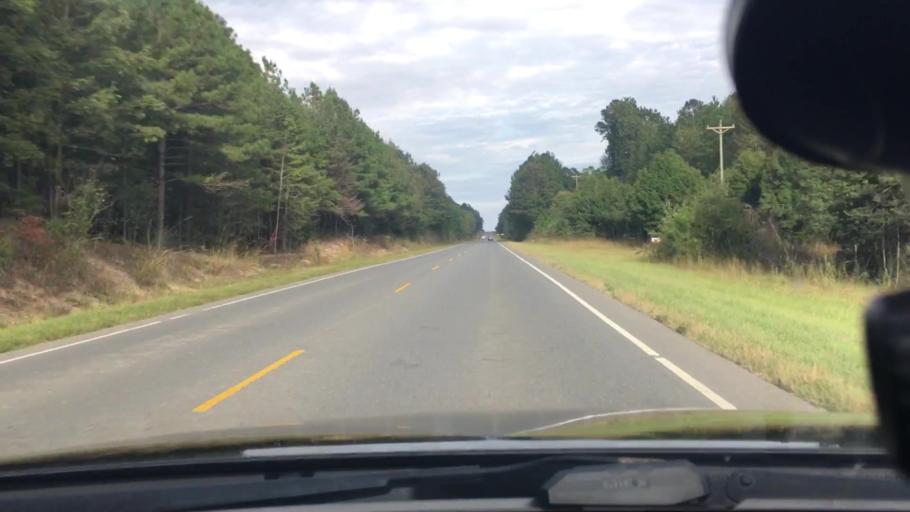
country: US
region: North Carolina
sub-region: Montgomery County
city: Troy
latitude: 35.3149
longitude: -79.9824
